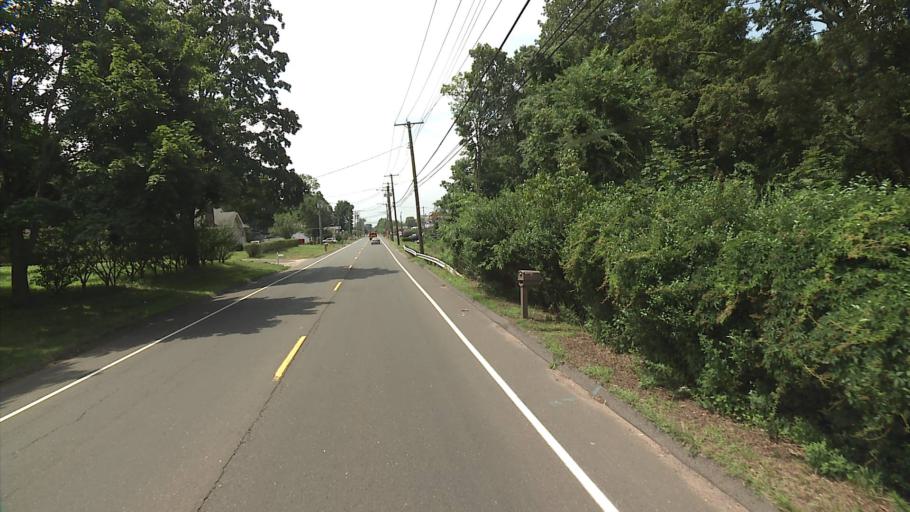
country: US
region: Connecticut
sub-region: New Haven County
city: North Haven
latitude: 41.3429
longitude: -72.8602
